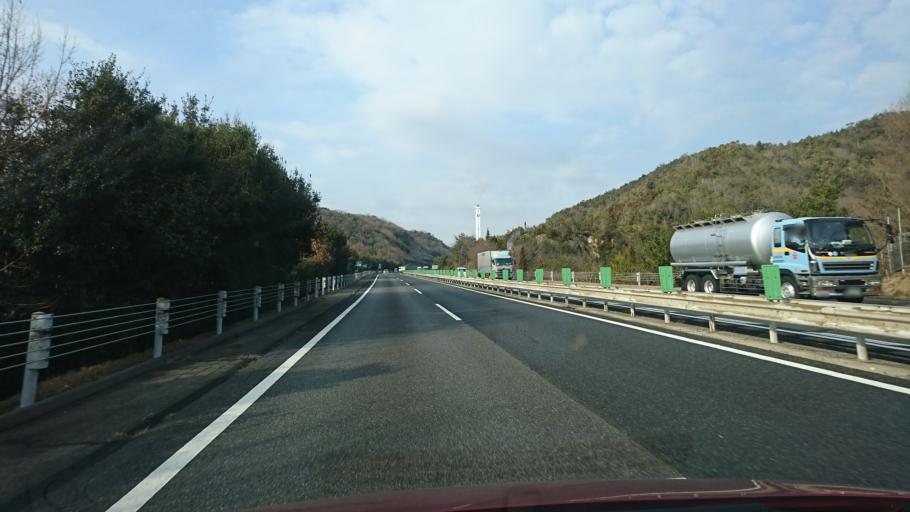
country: JP
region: Hyogo
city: Kariya
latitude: 34.7788
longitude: 134.2408
